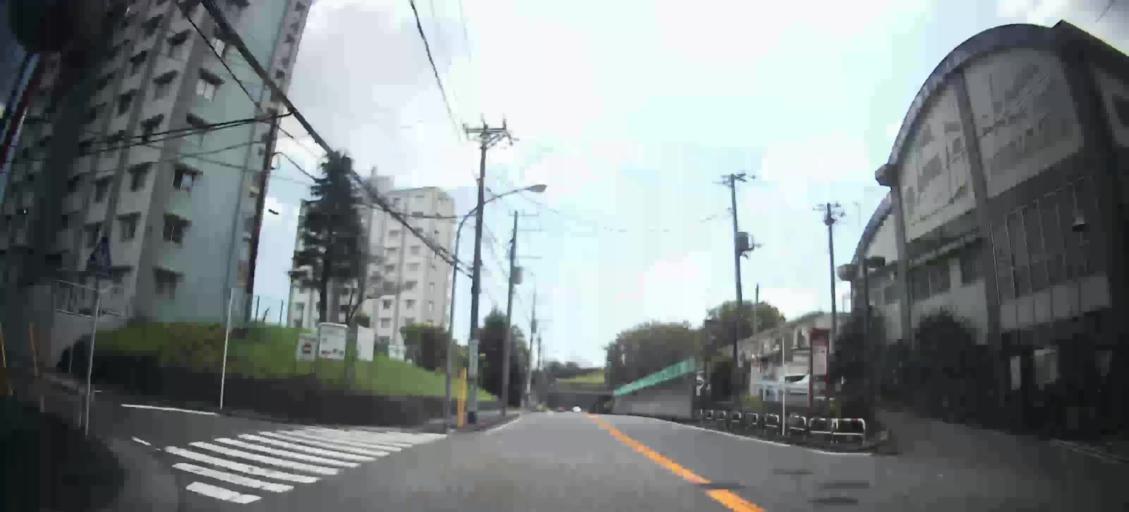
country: JP
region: Kanagawa
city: Yokohama
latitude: 35.4560
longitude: 139.5556
